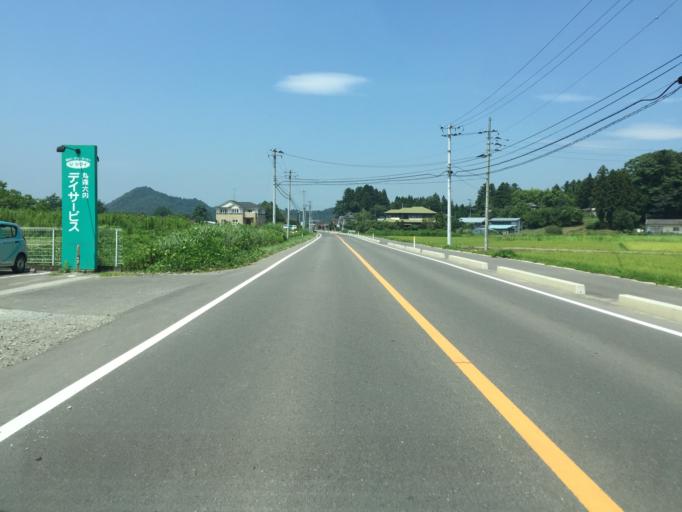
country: JP
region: Miyagi
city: Marumori
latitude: 37.8820
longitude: 140.8200
